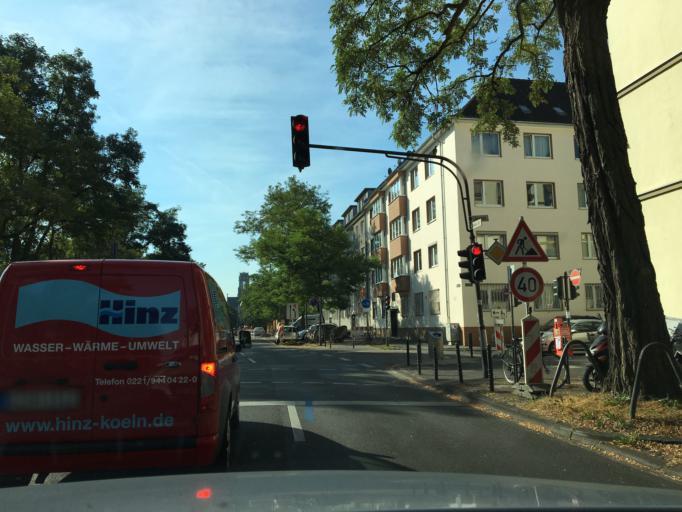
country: DE
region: North Rhine-Westphalia
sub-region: Regierungsbezirk Koln
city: Nippes
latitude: 50.9602
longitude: 6.9581
